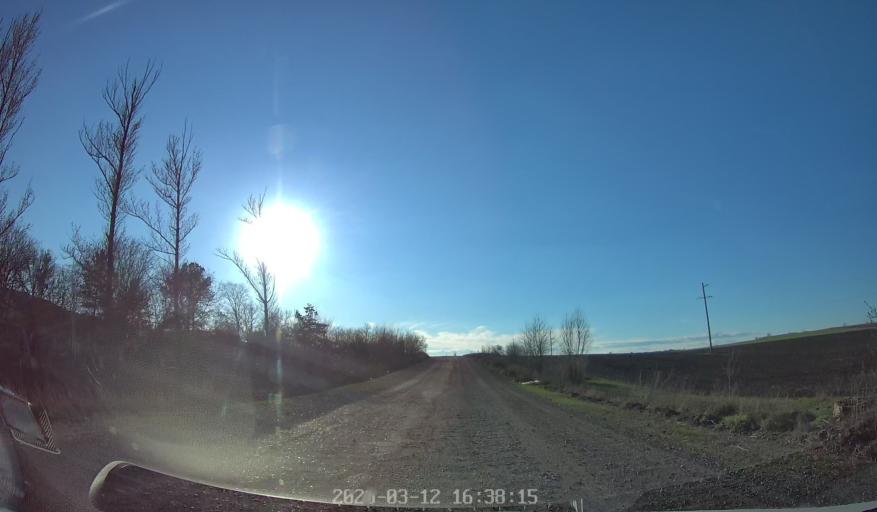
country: MD
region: Anenii Noi
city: Anenii Noi
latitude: 46.8155
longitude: 29.1811
